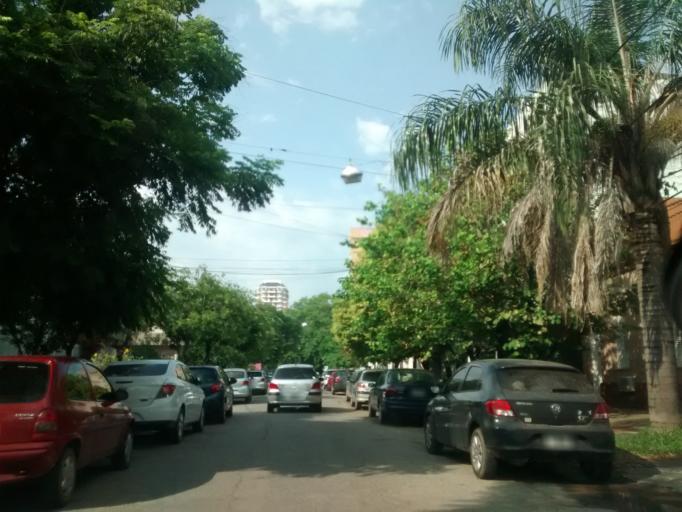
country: AR
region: Chaco
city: Resistencia
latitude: -27.4458
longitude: -58.9824
